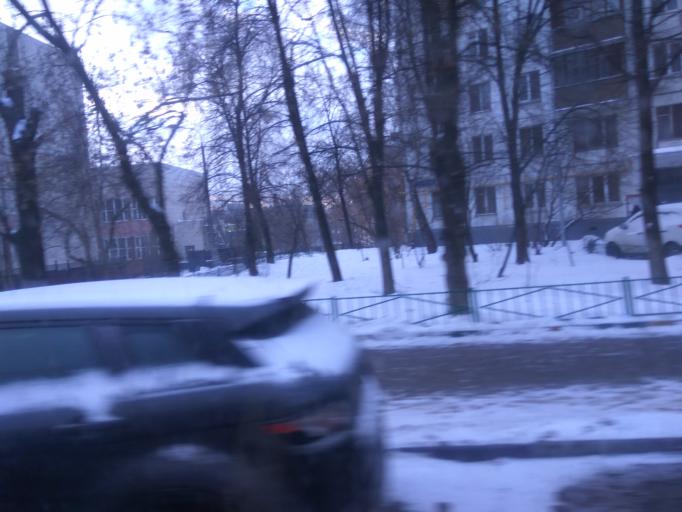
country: RU
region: Moscow
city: Sokol'niki
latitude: 55.7817
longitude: 37.6638
